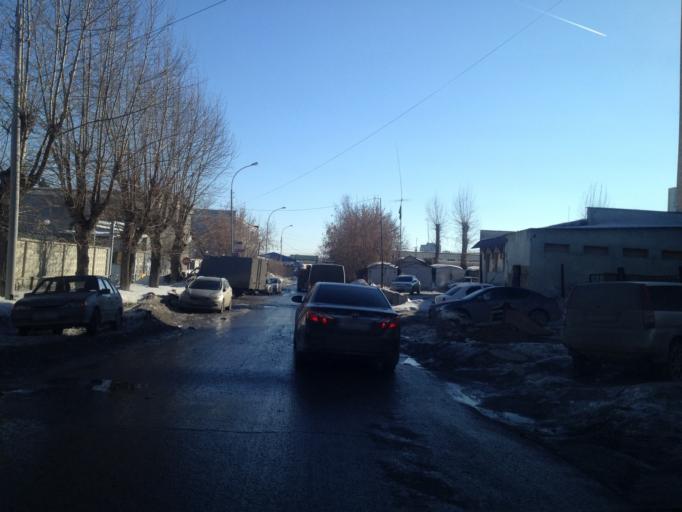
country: RU
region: Sverdlovsk
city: Yekaterinburg
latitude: 56.8374
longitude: 60.6648
